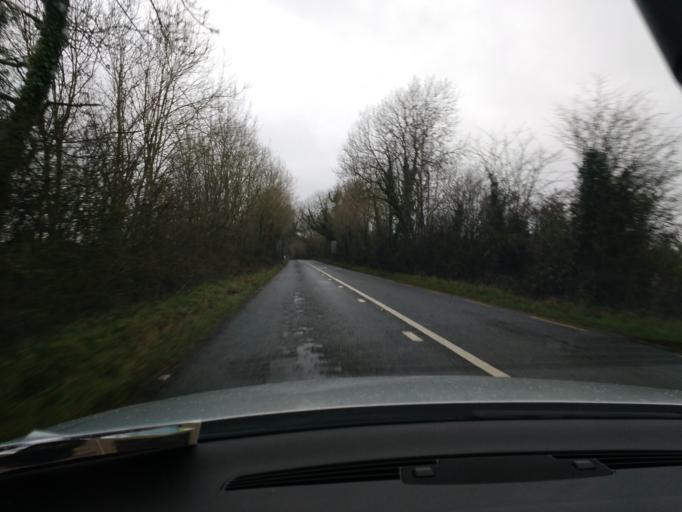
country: IE
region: Munster
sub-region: North Tipperary
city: Nenagh
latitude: 52.8290
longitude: -8.0929
